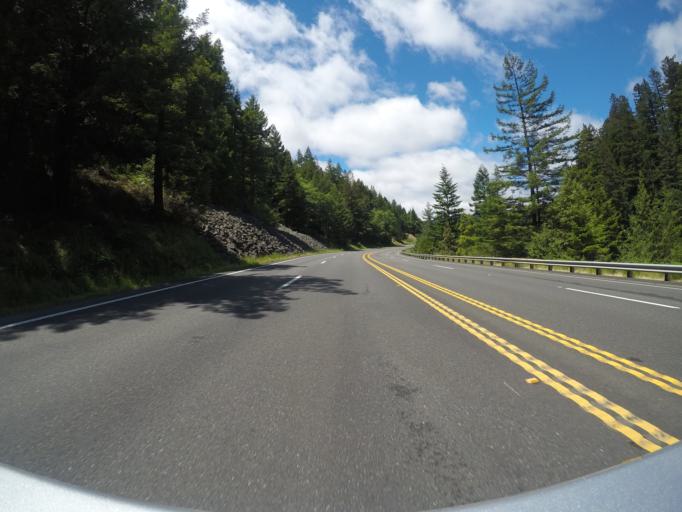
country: US
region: California
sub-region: Humboldt County
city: Redway
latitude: 40.2612
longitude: -123.8461
